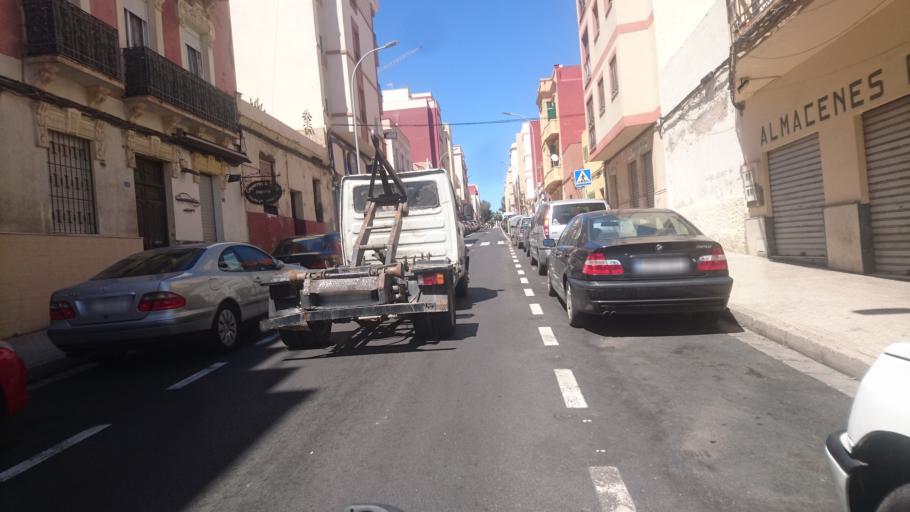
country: ES
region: Melilla
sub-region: Melilla
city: Melilla
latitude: 35.2959
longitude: -2.9418
